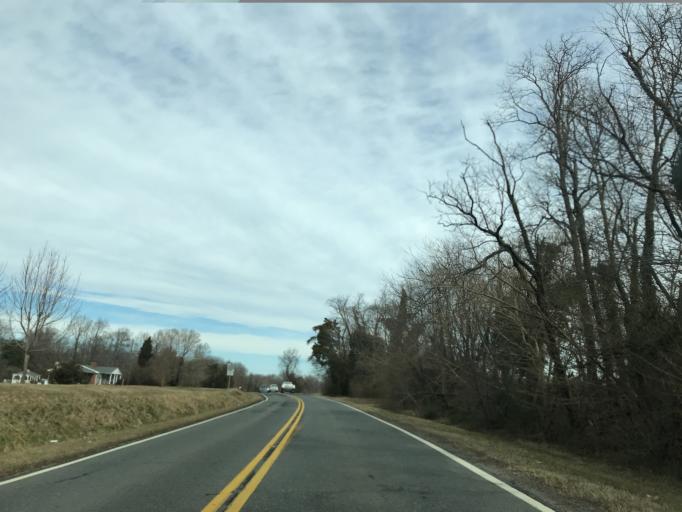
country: US
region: Virginia
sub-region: King George County
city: Dahlgren
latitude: 38.2765
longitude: -77.0456
